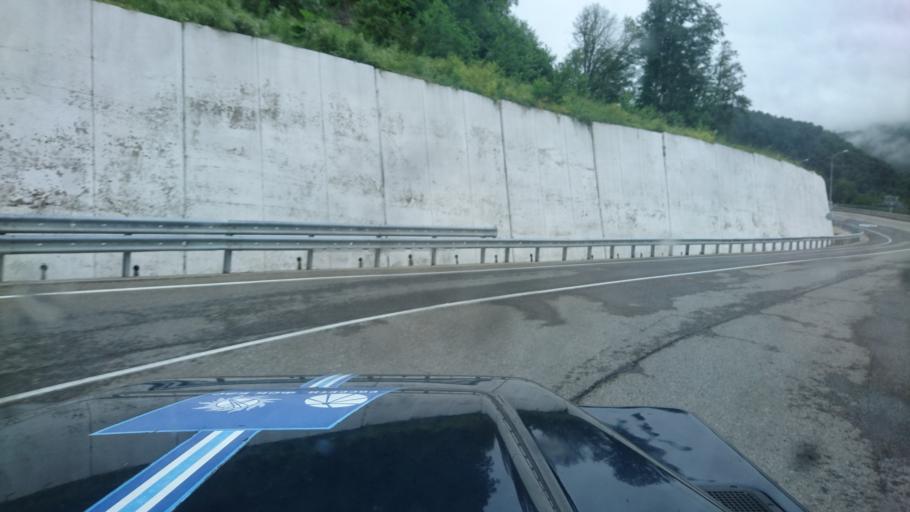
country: RU
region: Krasnodarskiy
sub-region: Sochi City
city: Krasnaya Polyana
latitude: 43.6646
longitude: 40.3125
